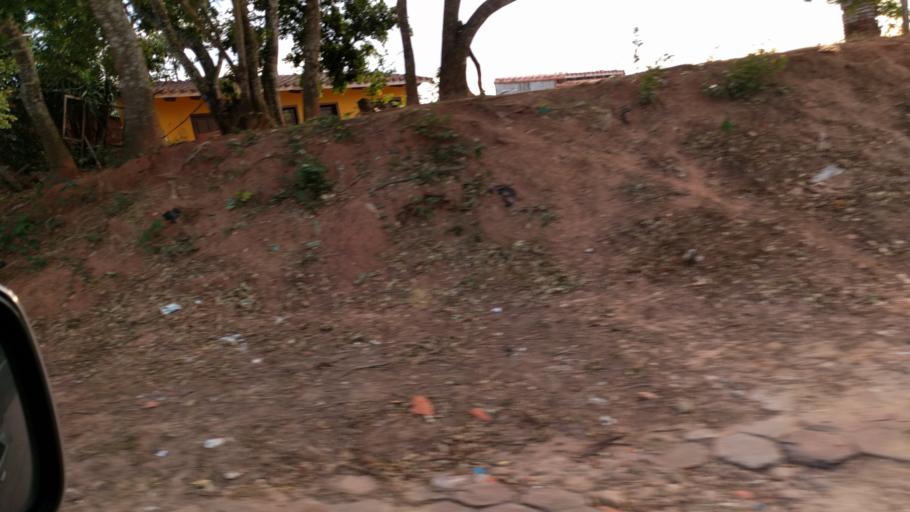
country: BO
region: Santa Cruz
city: Buena Vista
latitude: -17.4566
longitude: -63.6573
